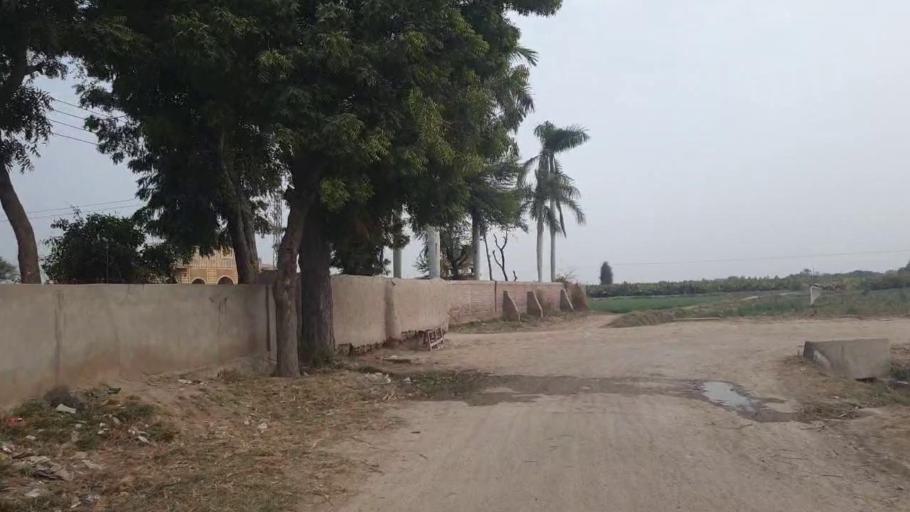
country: PK
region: Sindh
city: Shahdadpur
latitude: 25.9451
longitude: 68.7035
